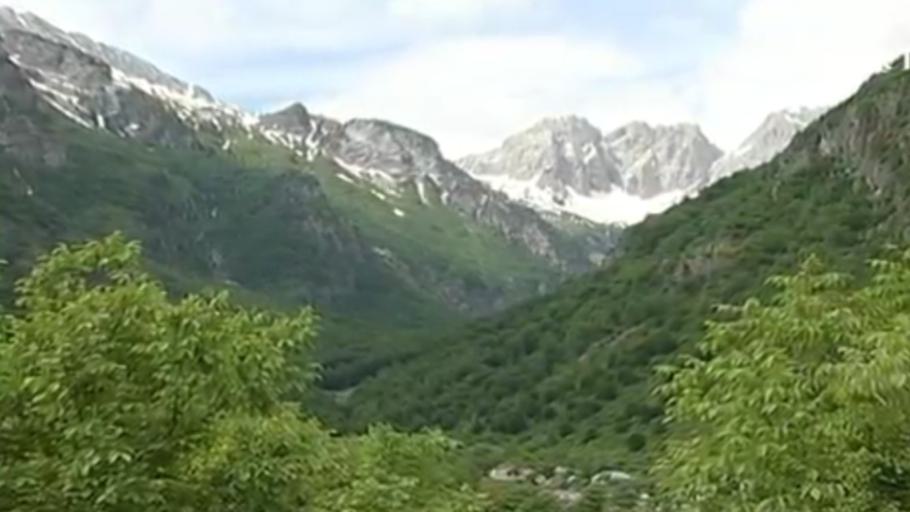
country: AL
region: Kukes
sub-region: Rrethi i Tropojes
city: Valbone
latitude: 42.4334
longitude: 19.9752
